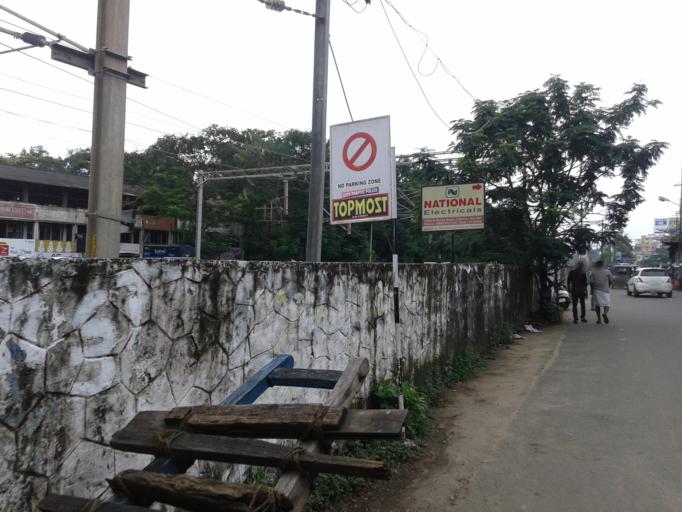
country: IN
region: Kerala
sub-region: Kozhikode
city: Kozhikode
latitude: 11.2490
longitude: 75.7803
